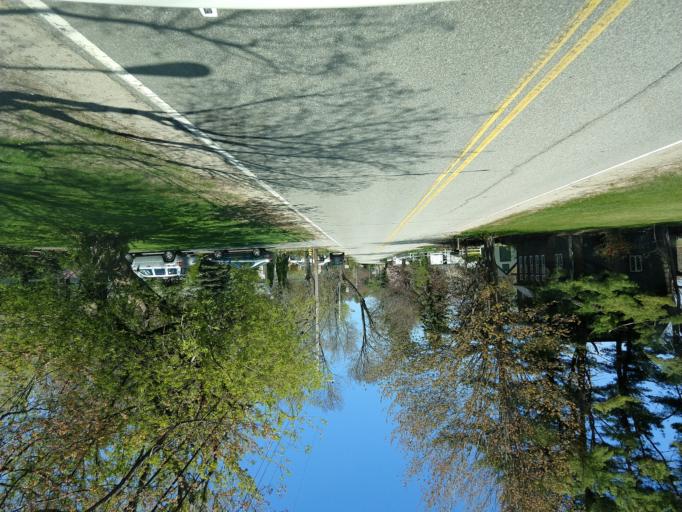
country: US
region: Maine
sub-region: York County
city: Old Orchard Beach
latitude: 43.4727
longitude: -70.3946
